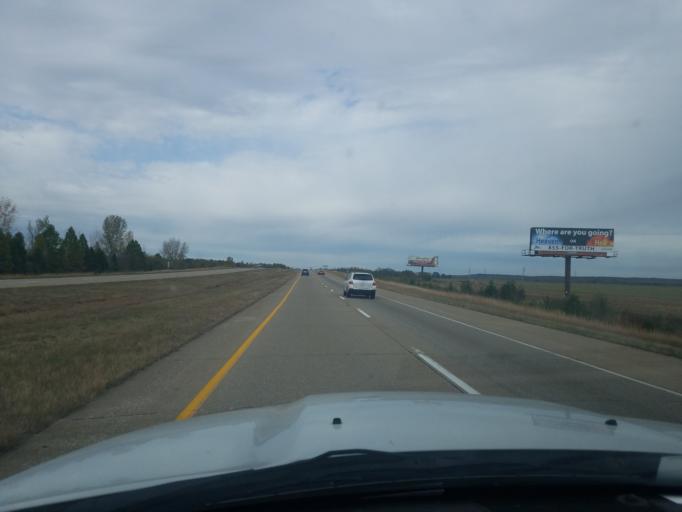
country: US
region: Indiana
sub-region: Vanderburgh County
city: Melody Hill
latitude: 38.0463
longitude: -87.4741
